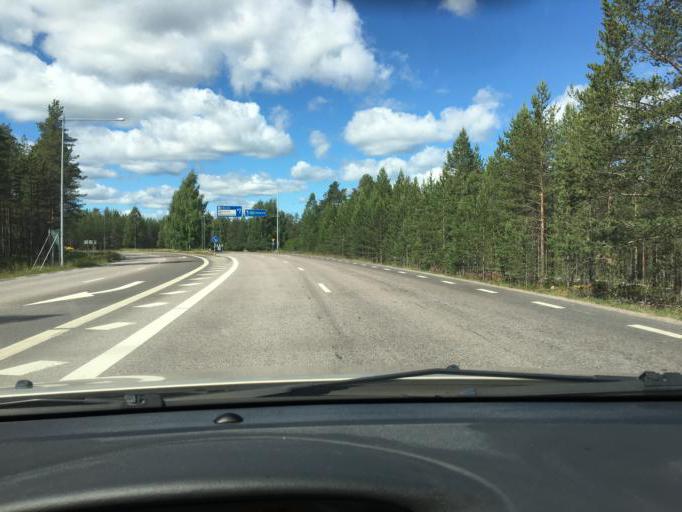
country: SE
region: Norrbotten
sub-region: Lulea Kommun
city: Bergnaset
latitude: 65.5794
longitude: 22.0786
